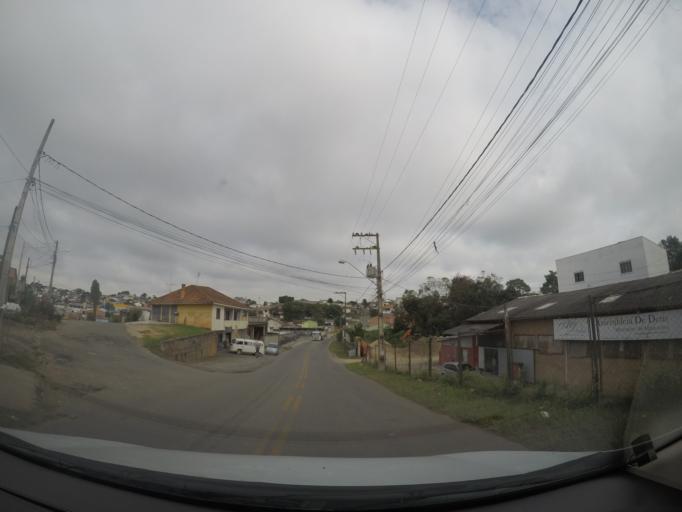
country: BR
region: Parana
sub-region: Colombo
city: Colombo
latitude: -25.3494
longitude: -49.2118
